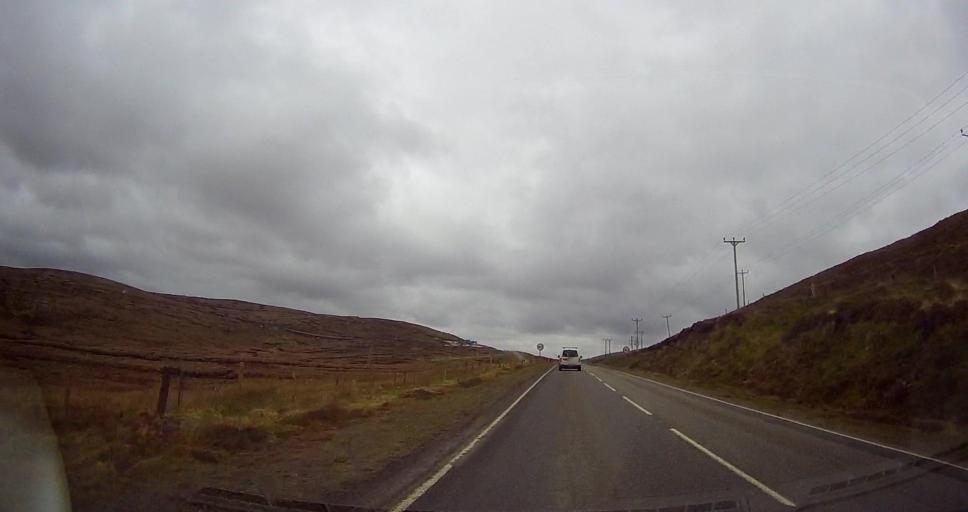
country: GB
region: Scotland
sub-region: Shetland Islands
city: Lerwick
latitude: 60.3331
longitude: -1.2541
